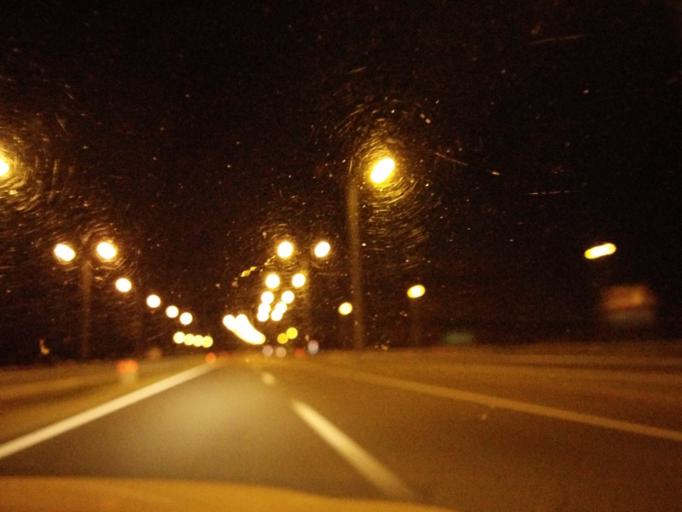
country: HR
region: Brodsko-Posavska
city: Vrpolje
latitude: 45.1450
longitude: 18.3076
